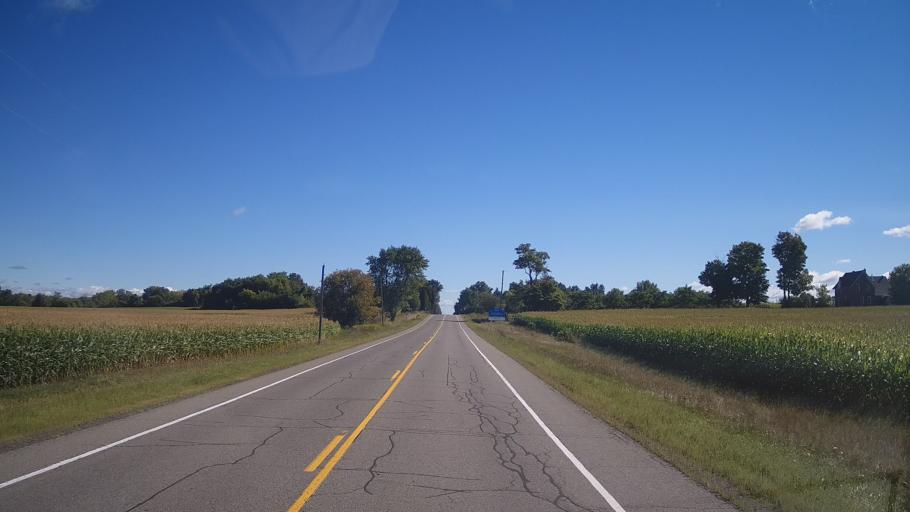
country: US
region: New York
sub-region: St. Lawrence County
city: Ogdensburg
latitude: 44.9379
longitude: -75.3130
